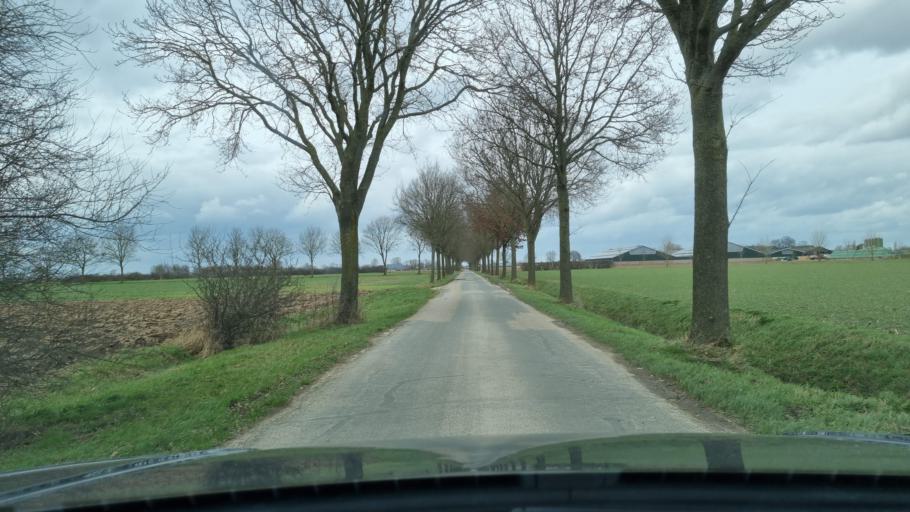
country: DE
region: North Rhine-Westphalia
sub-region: Regierungsbezirk Dusseldorf
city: Kranenburg
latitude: 51.8296
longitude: 6.0738
